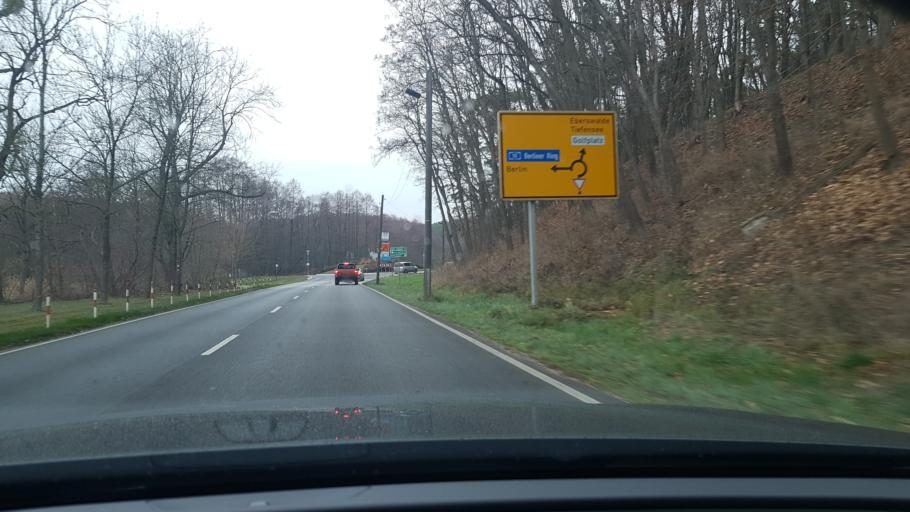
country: DE
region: Brandenburg
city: Strausberg
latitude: 52.5924
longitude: 13.8922
